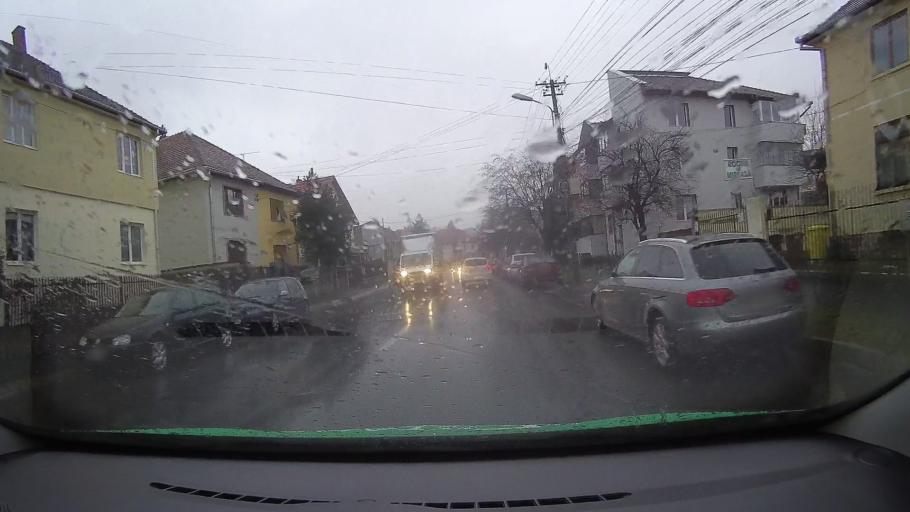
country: RO
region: Sibiu
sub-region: Municipiul Sibiu
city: Sibiu
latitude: 45.7947
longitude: 24.1401
